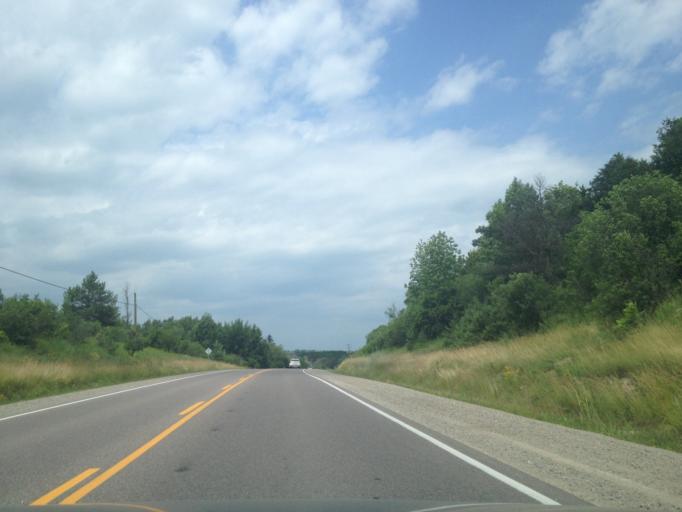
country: CA
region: Ontario
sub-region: Wellington County
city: Guelph
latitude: 43.5813
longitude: -80.2460
